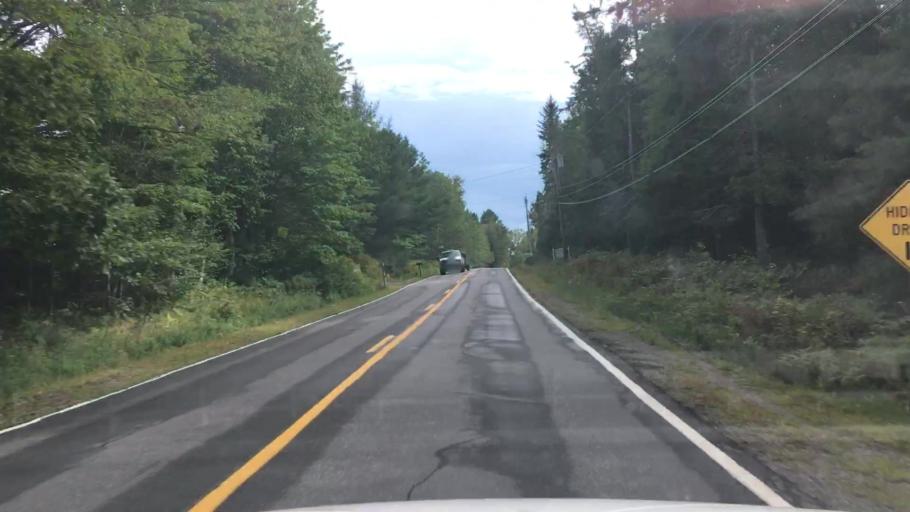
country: US
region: Maine
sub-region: Hancock County
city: Ellsworth
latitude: 44.4841
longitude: -68.4202
